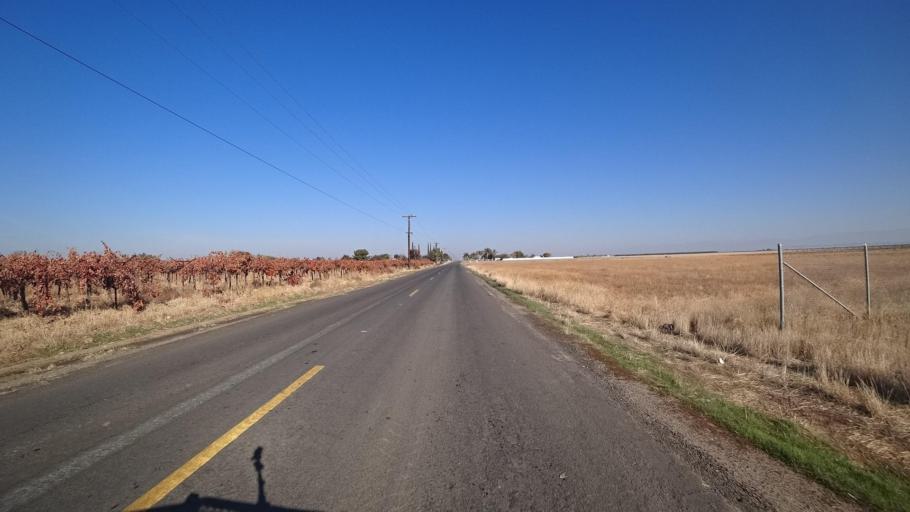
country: US
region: California
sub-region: Tulare County
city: Richgrove
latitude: 35.7452
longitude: -119.1343
